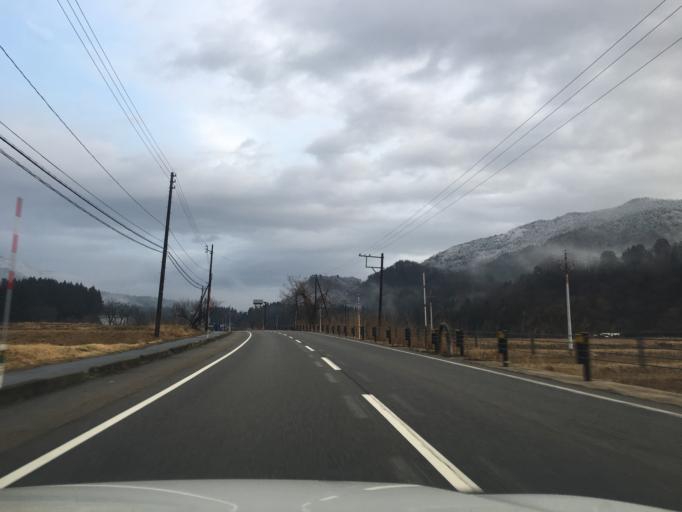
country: JP
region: Niigata
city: Murakami
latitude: 38.3573
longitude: 139.5522
